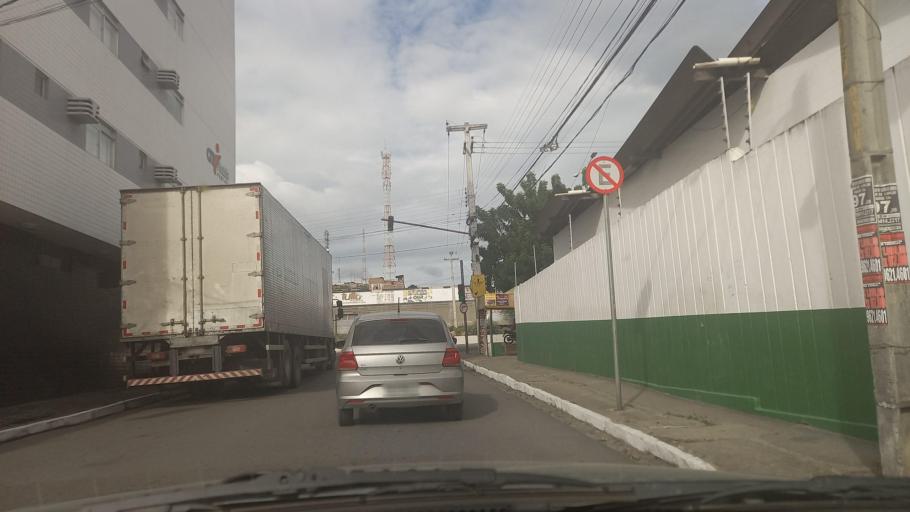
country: BR
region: Pernambuco
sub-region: Caruaru
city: Caruaru
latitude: -8.2859
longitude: -35.9844
